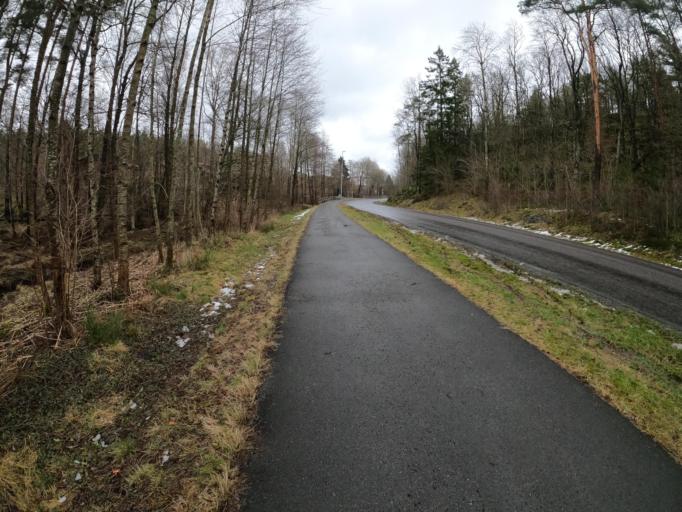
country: SE
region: Vaestra Goetaland
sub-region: Harryda Kommun
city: Molnlycke
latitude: 57.6437
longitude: 12.1144
